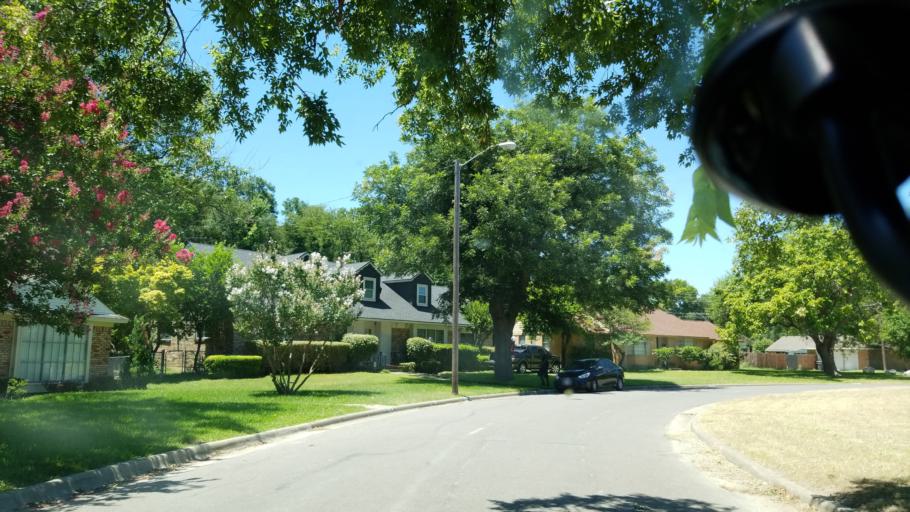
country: US
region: Texas
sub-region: Dallas County
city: Cockrell Hill
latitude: 32.6927
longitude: -96.8337
